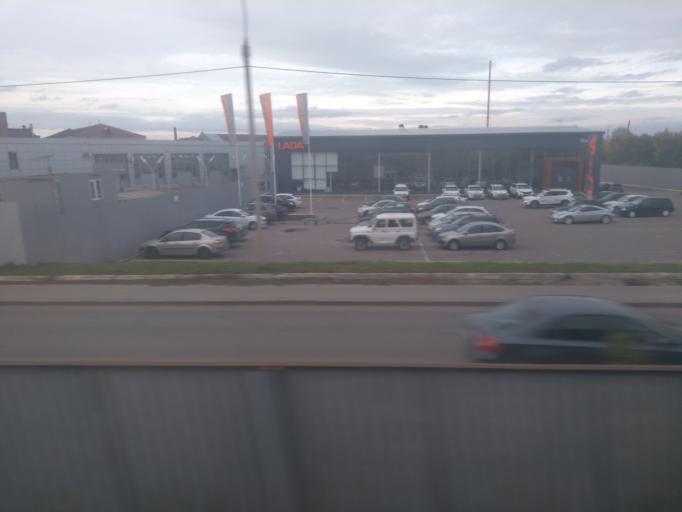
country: RU
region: Tatarstan
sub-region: Gorod Kazan'
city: Kazan
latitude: 55.8034
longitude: 49.0624
